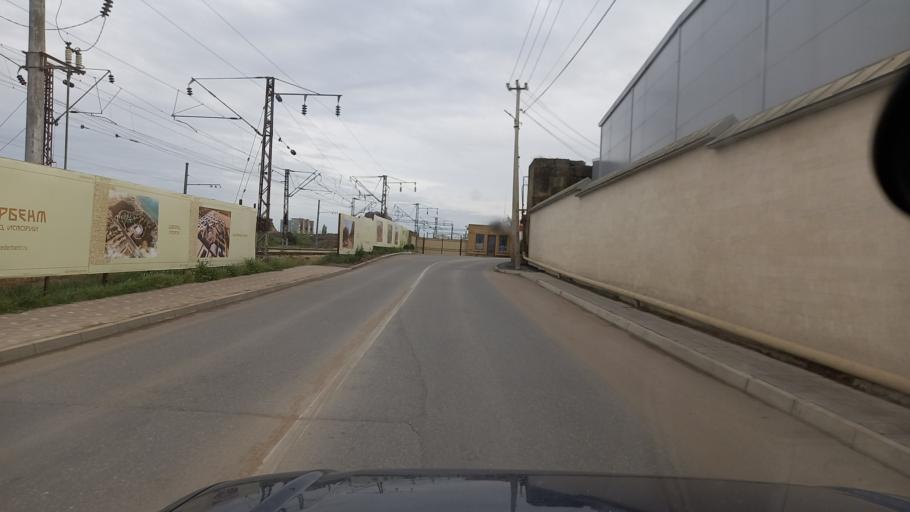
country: RU
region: Dagestan
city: Derbent
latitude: 42.0637
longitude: 48.3039
